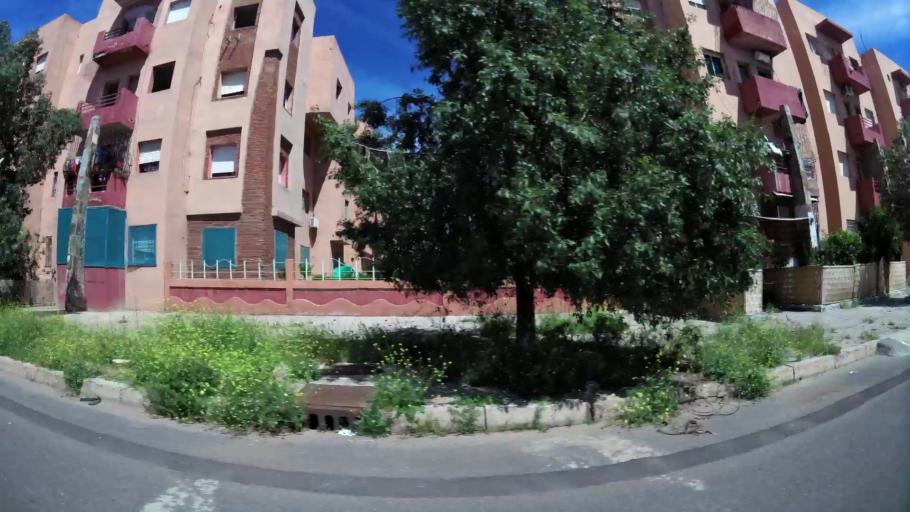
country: MA
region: Marrakech-Tensift-Al Haouz
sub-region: Marrakech
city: Marrakesh
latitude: 31.6426
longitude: -8.0813
